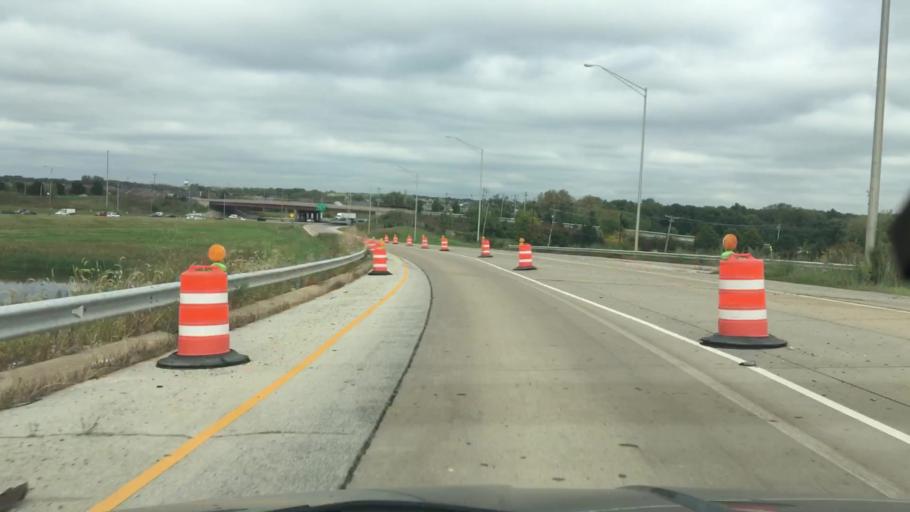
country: US
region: Illinois
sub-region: Cook County
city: Lemont
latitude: 41.7045
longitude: -88.0266
